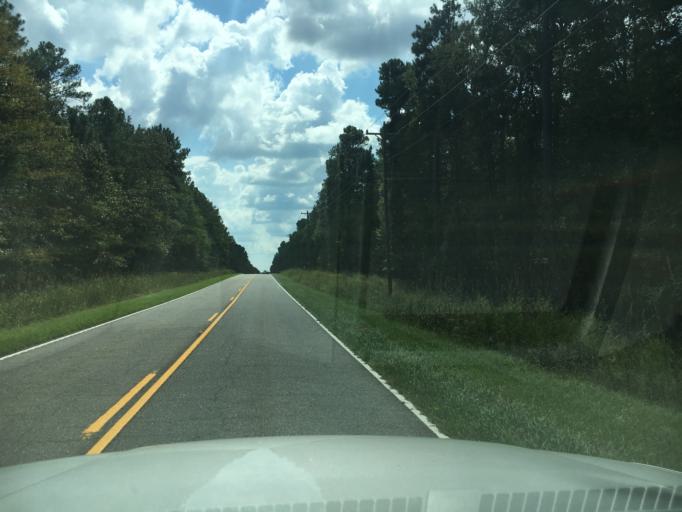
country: US
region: South Carolina
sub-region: Greenwood County
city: Greenwood
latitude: 34.0944
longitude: -82.1298
